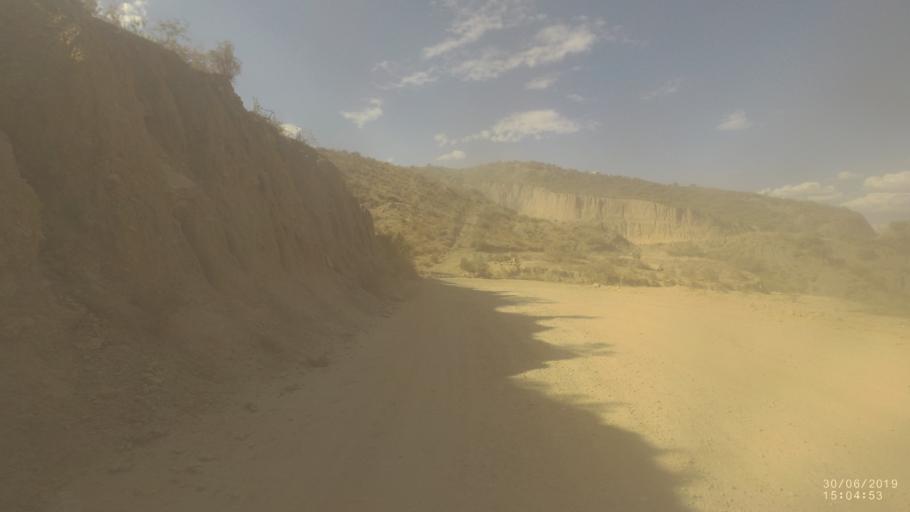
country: BO
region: Cochabamba
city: Irpa Irpa
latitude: -17.7323
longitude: -66.3190
